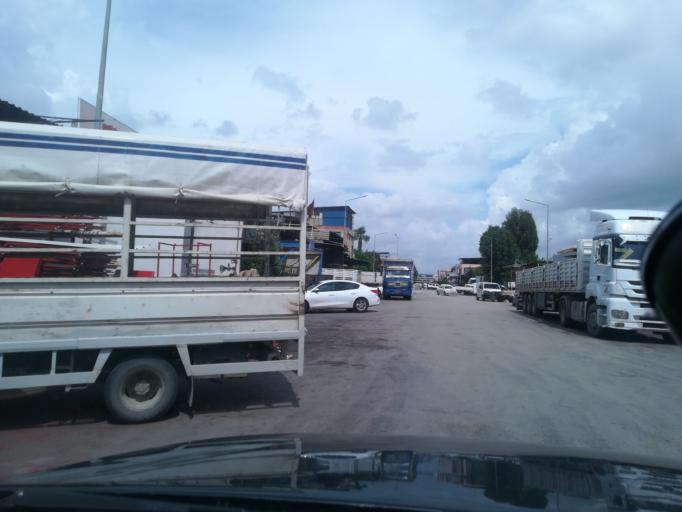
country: TR
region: Adana
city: Seyhan
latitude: 36.9824
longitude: 35.2542
